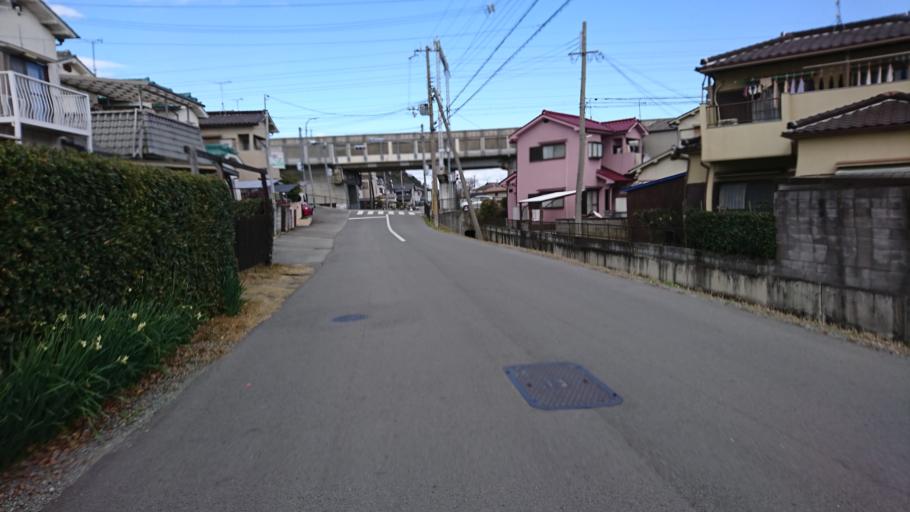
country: JP
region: Hyogo
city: Kakogawacho-honmachi
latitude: 34.7701
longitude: 134.7940
